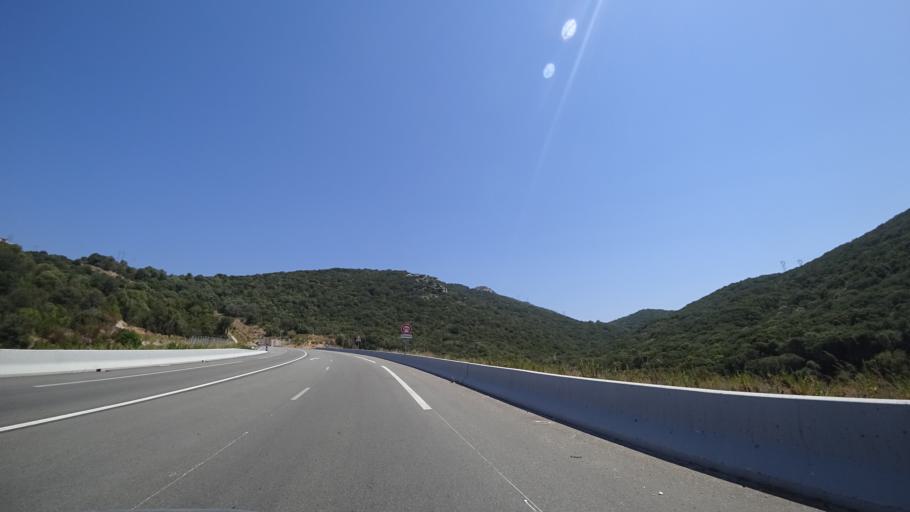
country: FR
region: Corsica
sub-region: Departement de la Corse-du-Sud
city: Propriano
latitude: 41.6682
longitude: 8.9252
